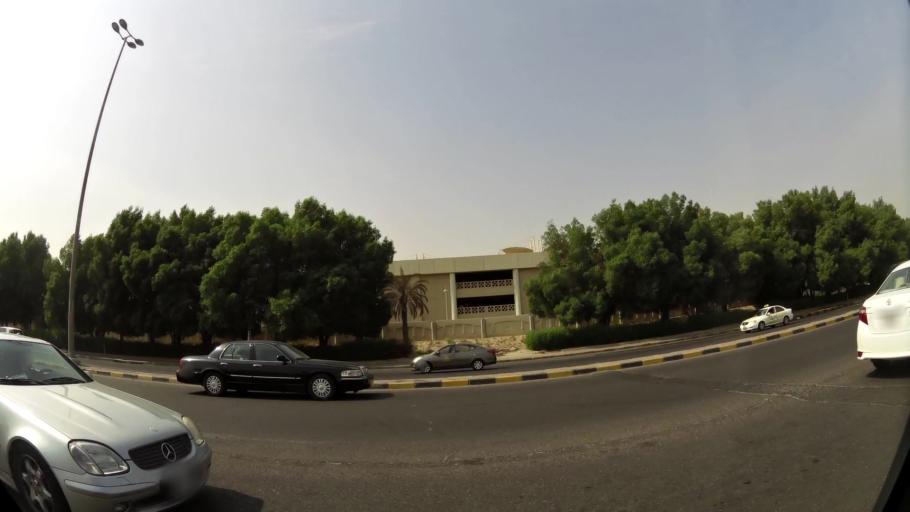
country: KW
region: Al Asimah
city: Ar Rabiyah
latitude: 29.2775
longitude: 47.9072
